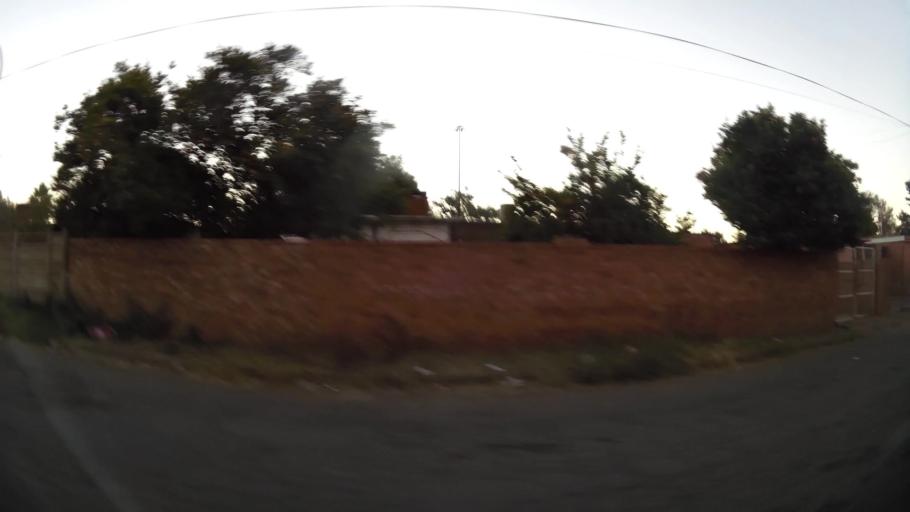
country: ZA
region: Northern Cape
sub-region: Frances Baard District Municipality
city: Kimberley
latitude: -28.7283
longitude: 24.7660
